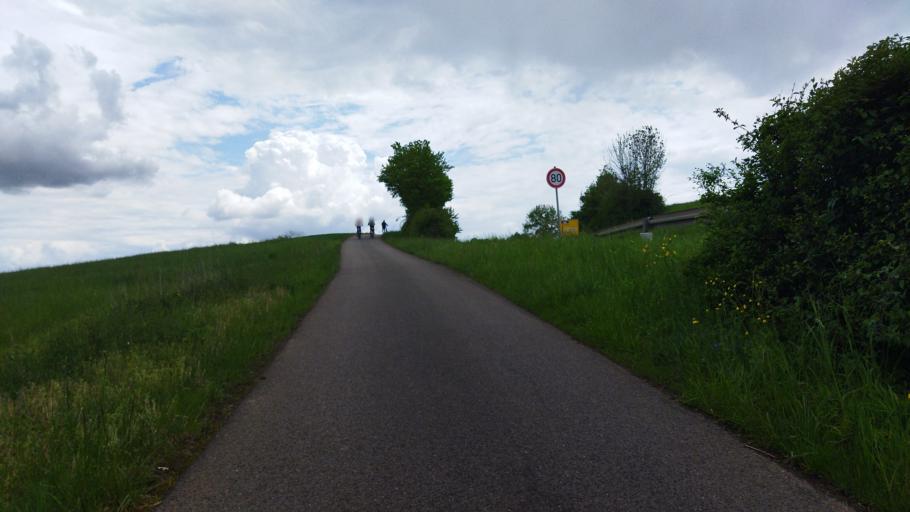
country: DE
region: Baden-Wuerttemberg
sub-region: Regierungsbezirk Stuttgart
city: Neckarwestheim
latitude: 49.0275
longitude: 9.1844
